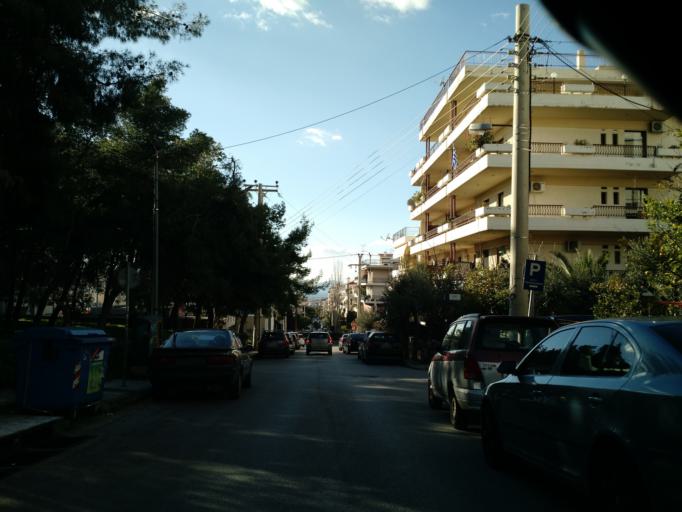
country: GR
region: Attica
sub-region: Nomarchia Athinas
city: Argyroupoli
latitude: 37.9155
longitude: 23.7559
